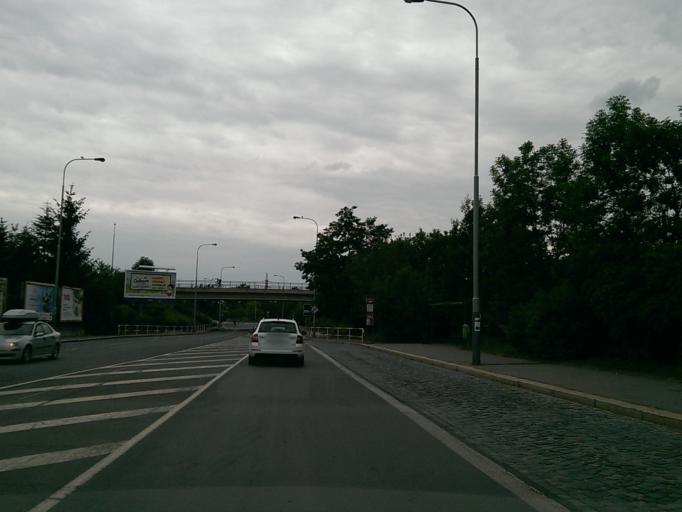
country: CZ
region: Praha
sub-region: Praha 14
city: Dolni Pocernice
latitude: 50.0477
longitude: 14.5654
